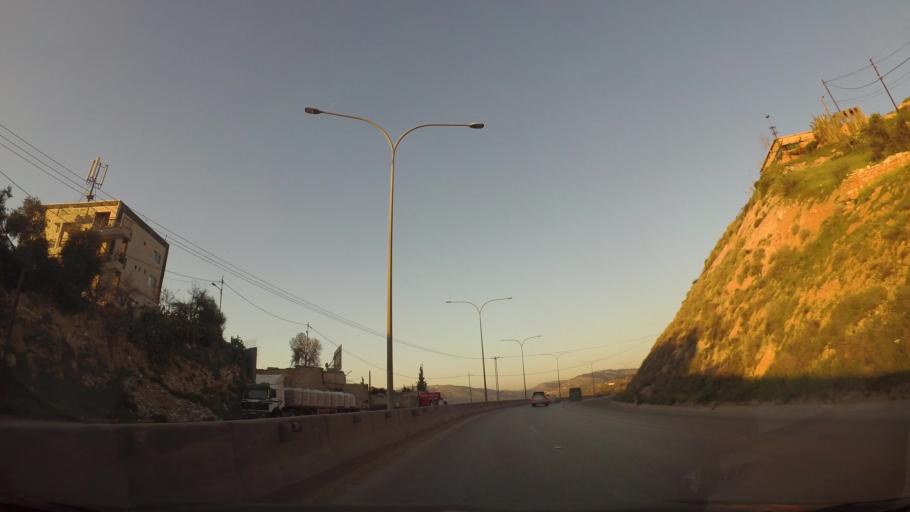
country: JO
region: Amman
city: Umm as Summaq
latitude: 31.8670
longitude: 35.7631
